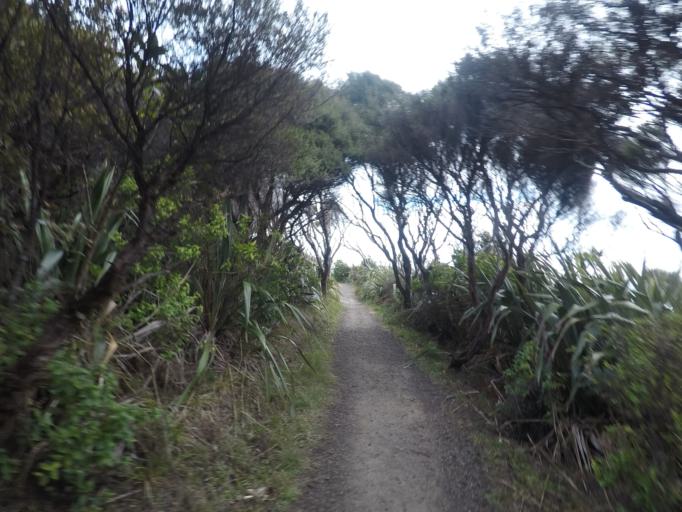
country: NZ
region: Auckland
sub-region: Auckland
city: Muriwai Beach
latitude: -36.9692
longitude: 174.4674
